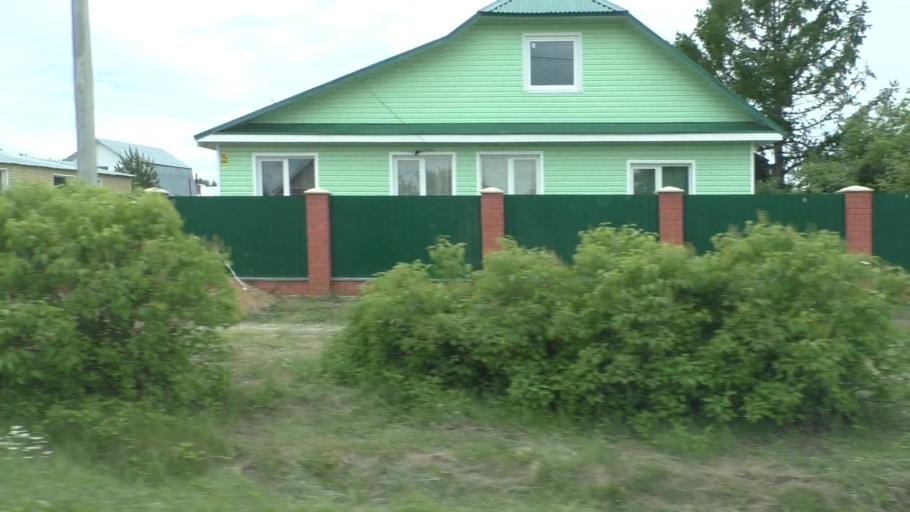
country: RU
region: Moskovskaya
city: Il'inskiy Pogost
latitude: 55.5022
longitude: 38.7951
